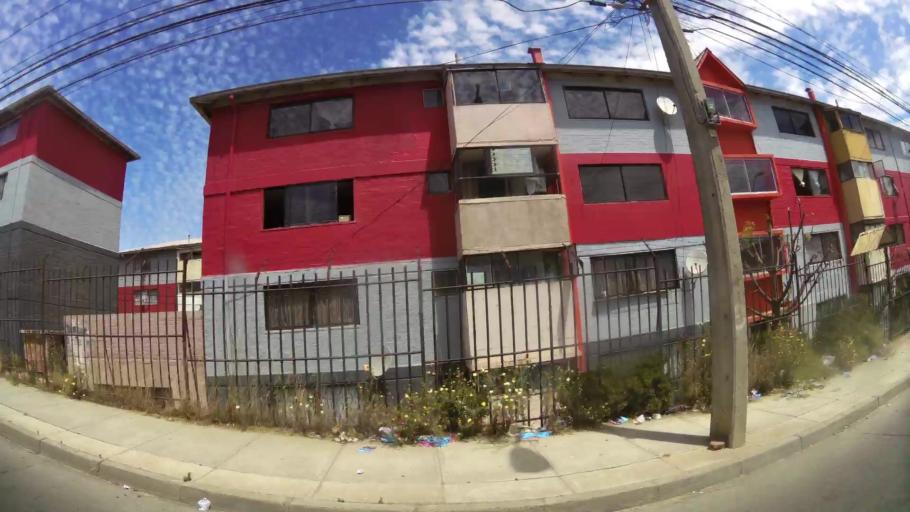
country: CL
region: Valparaiso
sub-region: Provincia de Valparaiso
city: Vina del Mar
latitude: -33.0661
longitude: -71.5674
